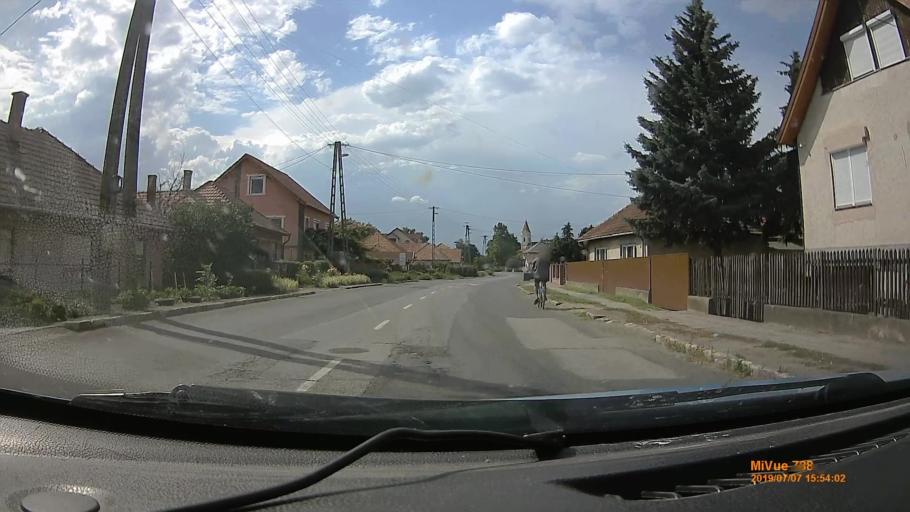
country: HU
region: Pest
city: Szentlorinckata
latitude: 47.5525
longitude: 19.7988
